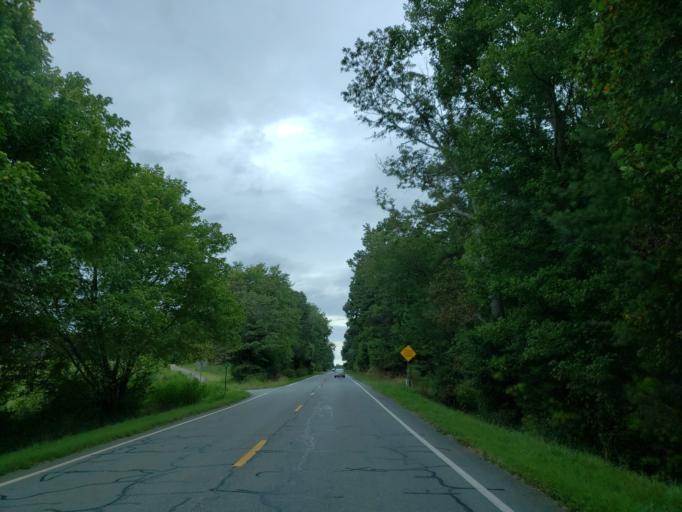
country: US
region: Georgia
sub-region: Gilmer County
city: Ellijay
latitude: 34.6401
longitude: -84.5350
